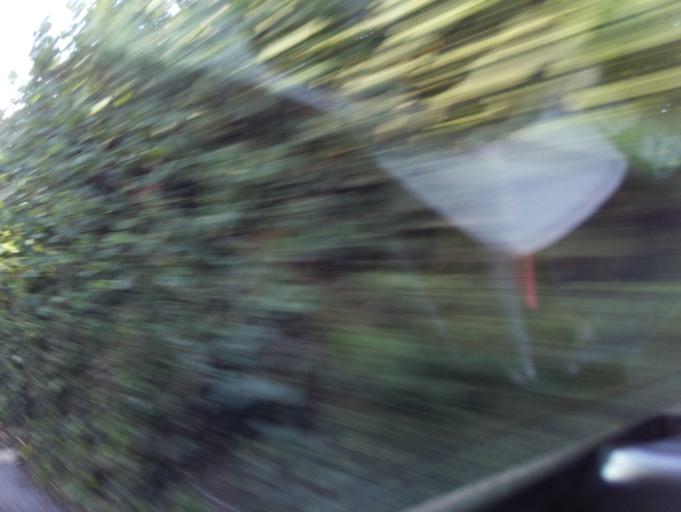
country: GB
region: England
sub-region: Devon
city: Dartmouth
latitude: 50.3316
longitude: -3.5999
